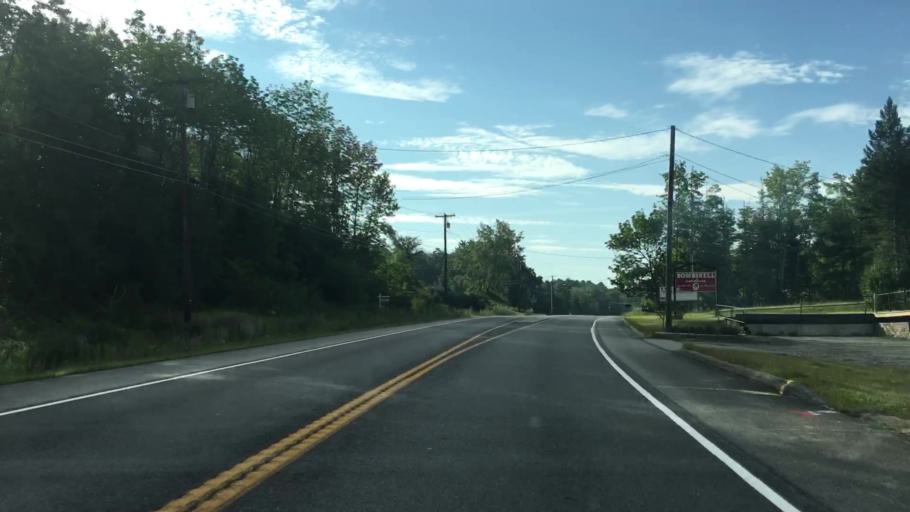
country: US
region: Maine
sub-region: Cumberland County
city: South Windham
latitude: 43.7801
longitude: -70.3865
